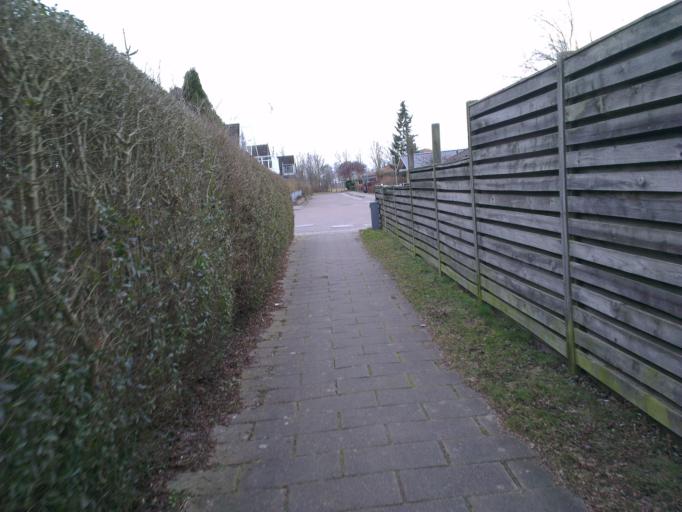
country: DK
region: Capital Region
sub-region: Frederikssund Kommune
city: Frederikssund
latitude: 55.8214
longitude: 12.0673
